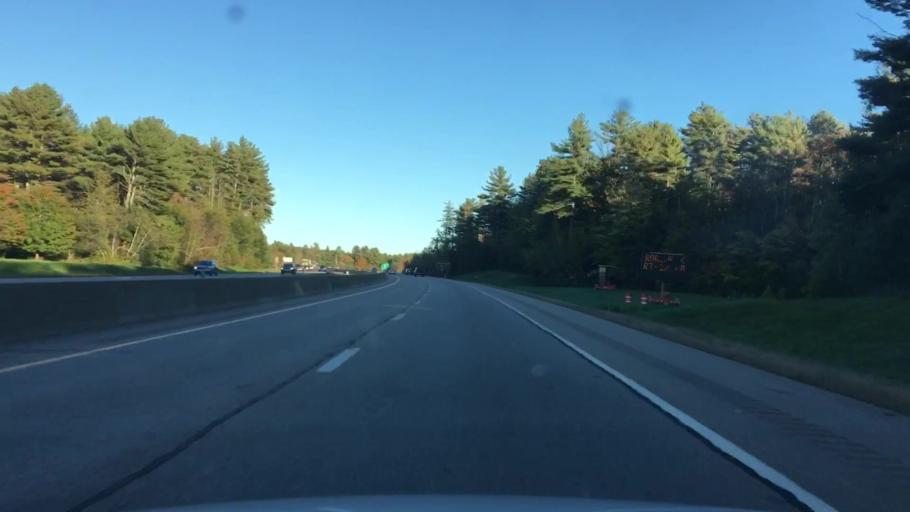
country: US
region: New Hampshire
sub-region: Rockingham County
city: Exeter
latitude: 43.0074
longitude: -70.9977
